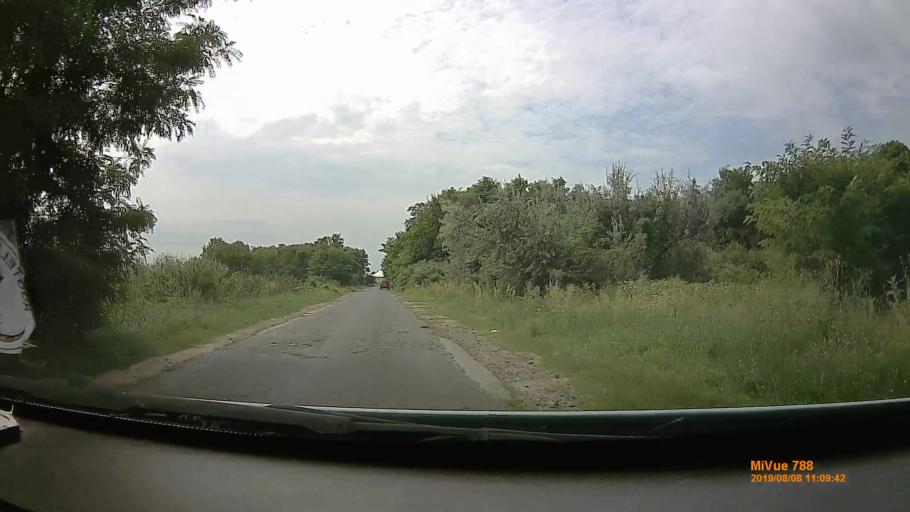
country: HU
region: Szabolcs-Szatmar-Bereg
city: Balkany
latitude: 47.7506
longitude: 21.8432
